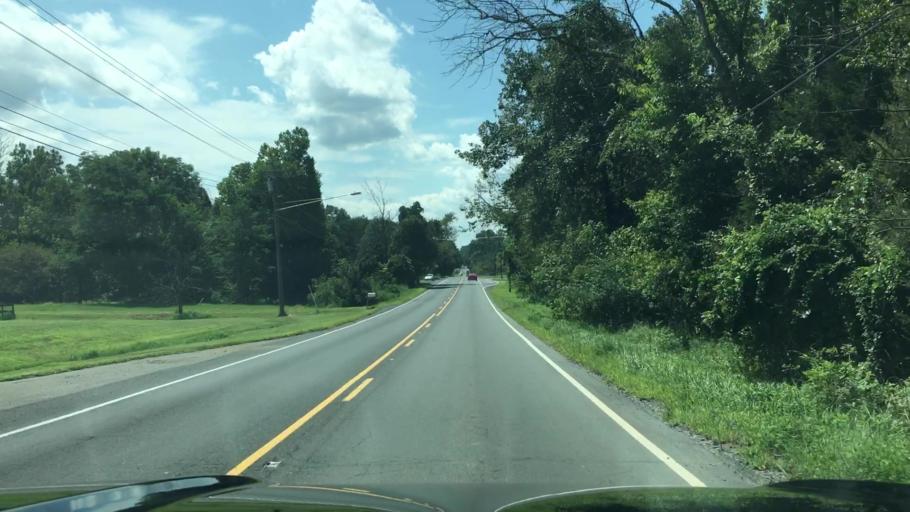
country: US
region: Virginia
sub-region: Prince William County
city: Sudley
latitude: 38.8252
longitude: -77.4989
